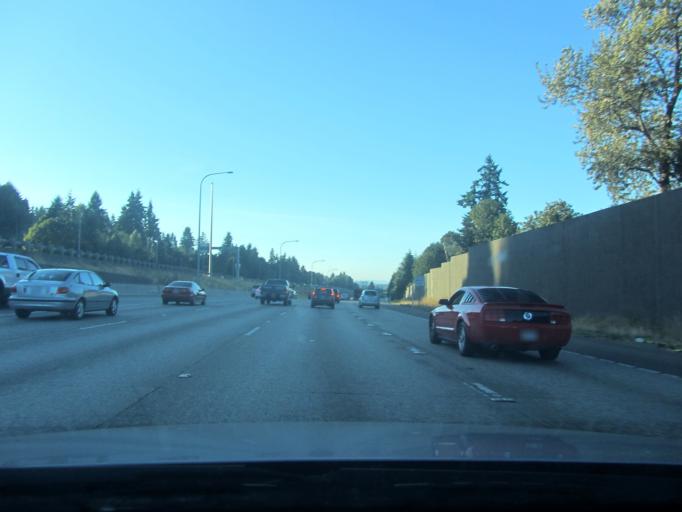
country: US
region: Washington
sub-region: Snohomish County
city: Everett
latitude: 47.9493
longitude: -122.1988
